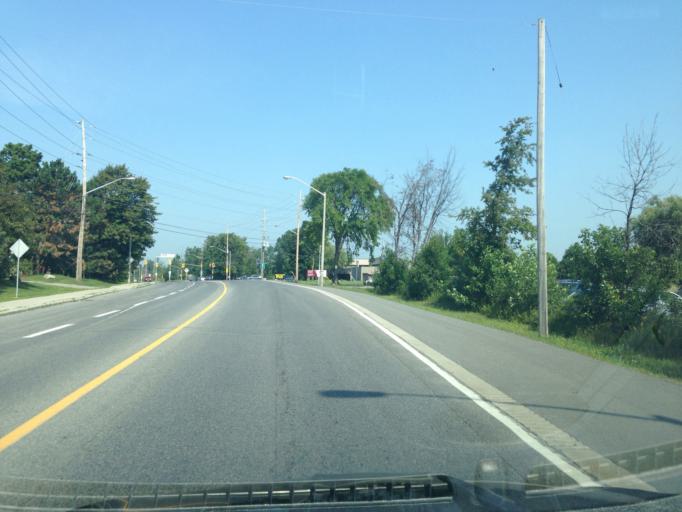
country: CA
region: Ontario
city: Ottawa
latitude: 45.4256
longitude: -75.5990
